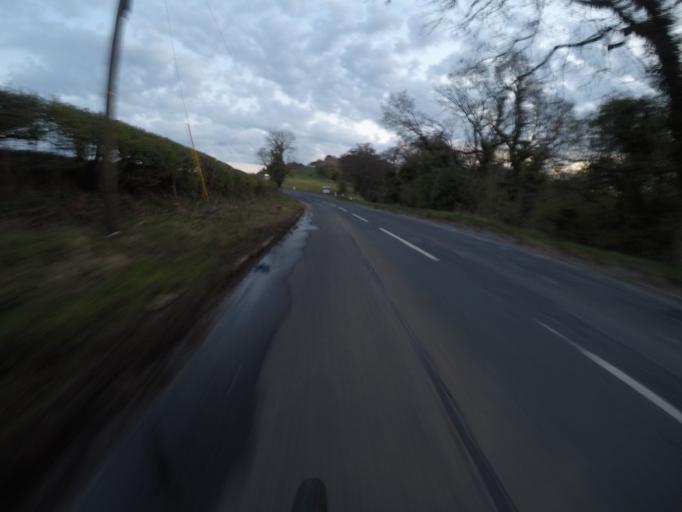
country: GB
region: Scotland
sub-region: South Ayrshire
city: Dundonald
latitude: 55.5687
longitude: -4.5997
